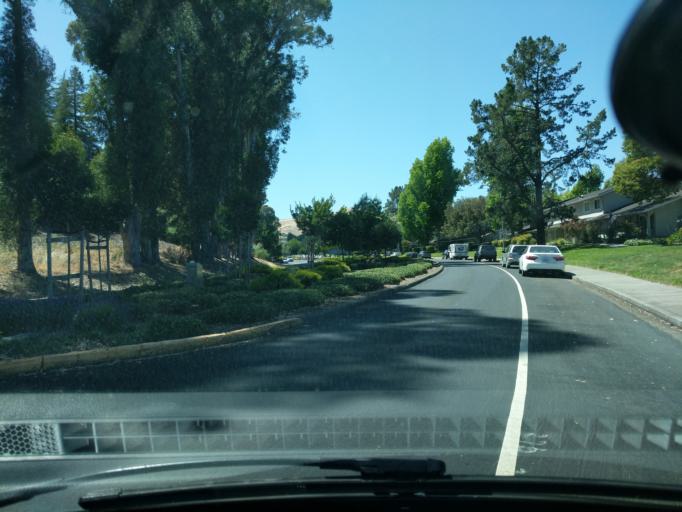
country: US
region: California
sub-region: Contra Costa County
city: San Ramon
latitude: 37.7680
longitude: -121.9888
